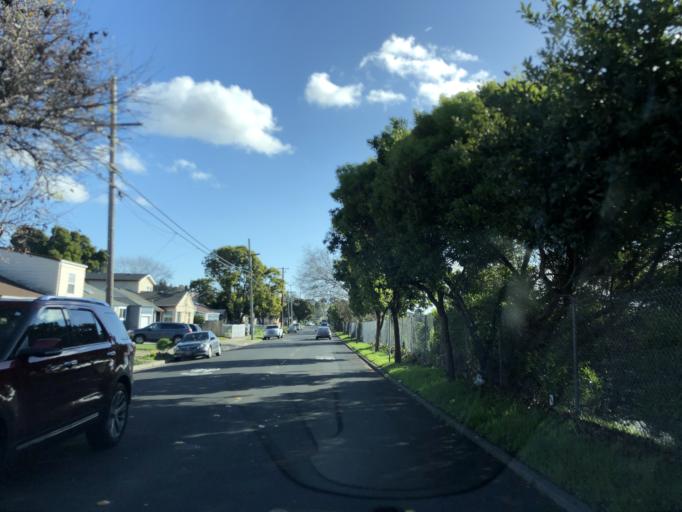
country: US
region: California
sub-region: Contra Costa County
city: East Richmond Heights
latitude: 37.9469
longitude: -122.3248
